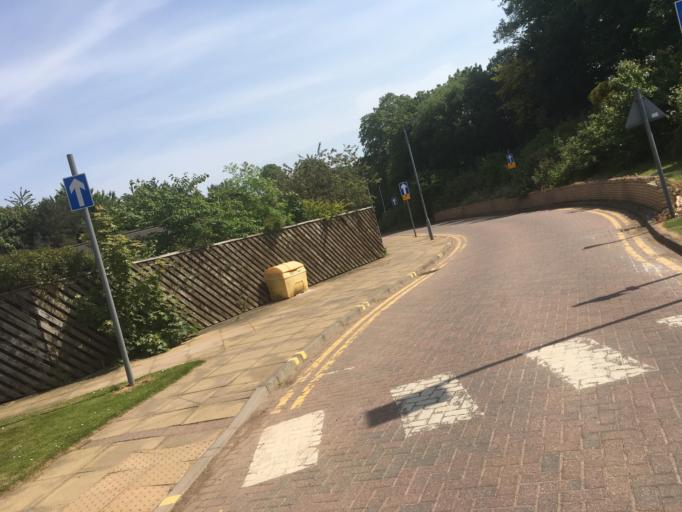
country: GB
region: Scotland
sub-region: Edinburgh
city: Edinburgh
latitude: 55.9286
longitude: -3.2165
